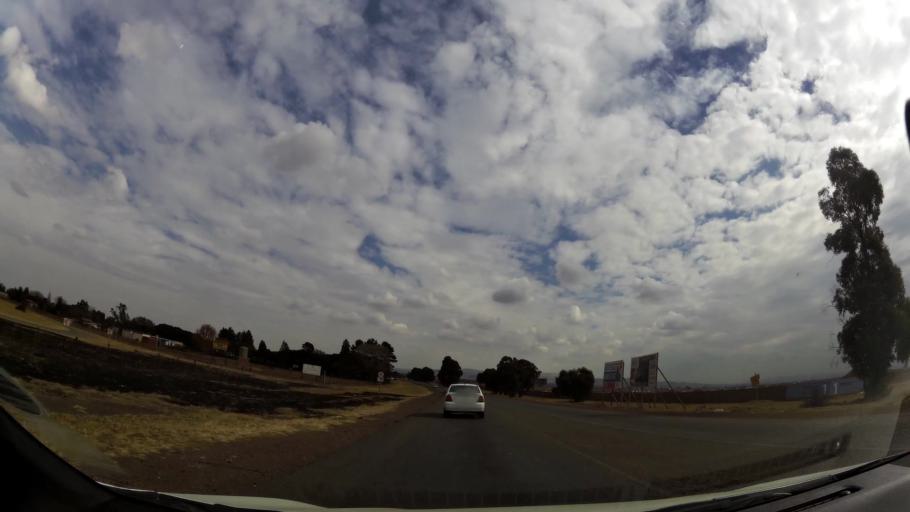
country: ZA
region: Gauteng
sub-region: Sedibeng District Municipality
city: Meyerton
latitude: -26.4192
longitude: 28.1176
